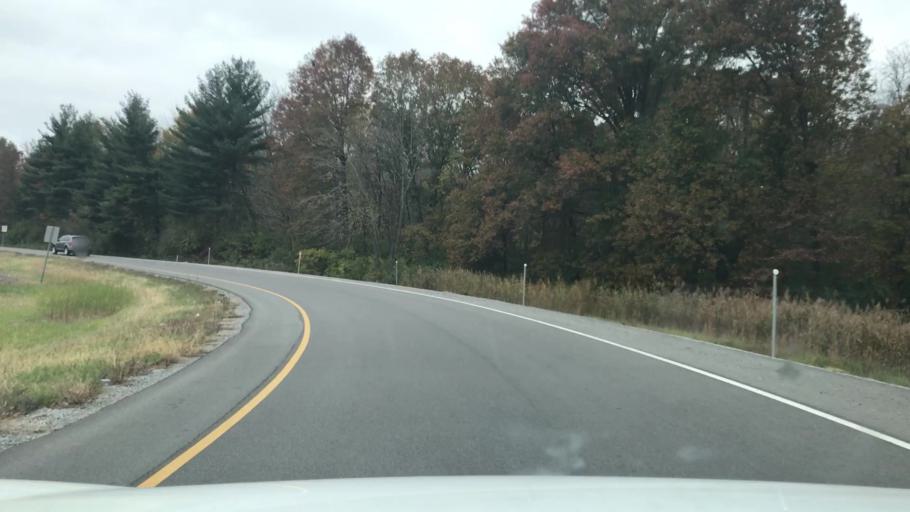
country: US
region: Illinois
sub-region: Jefferson County
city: Mount Vernon
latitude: 38.2754
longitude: -88.9042
